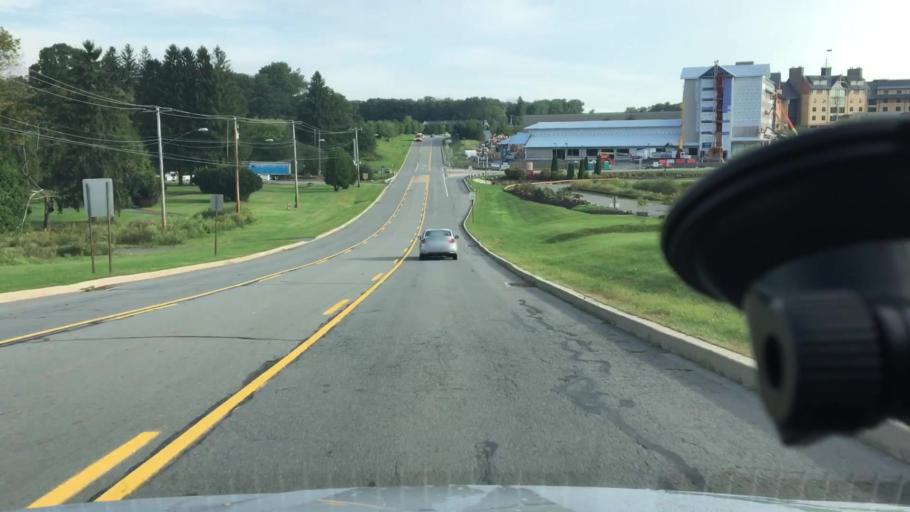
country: US
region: Pennsylvania
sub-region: Monroe County
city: Mount Pocono
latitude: 41.1104
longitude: -75.3247
